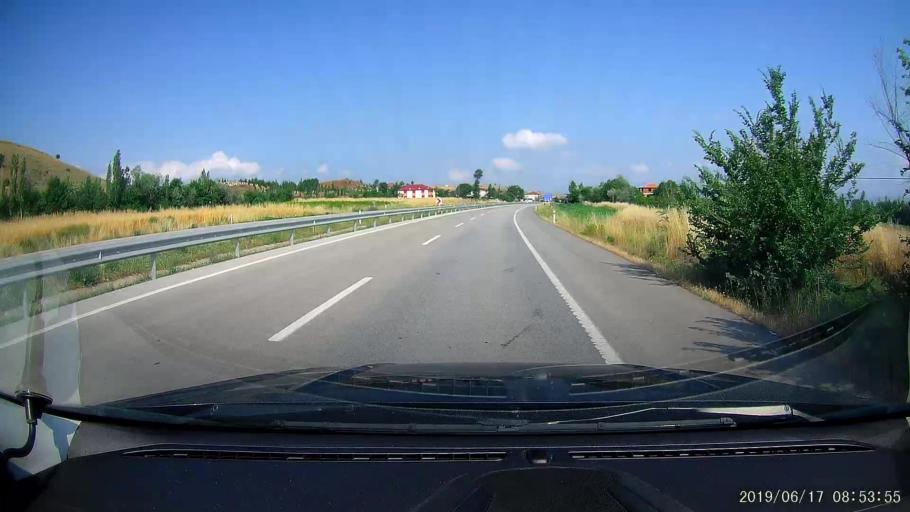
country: TR
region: Amasya
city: Esencay
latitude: 40.7140
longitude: 36.4714
